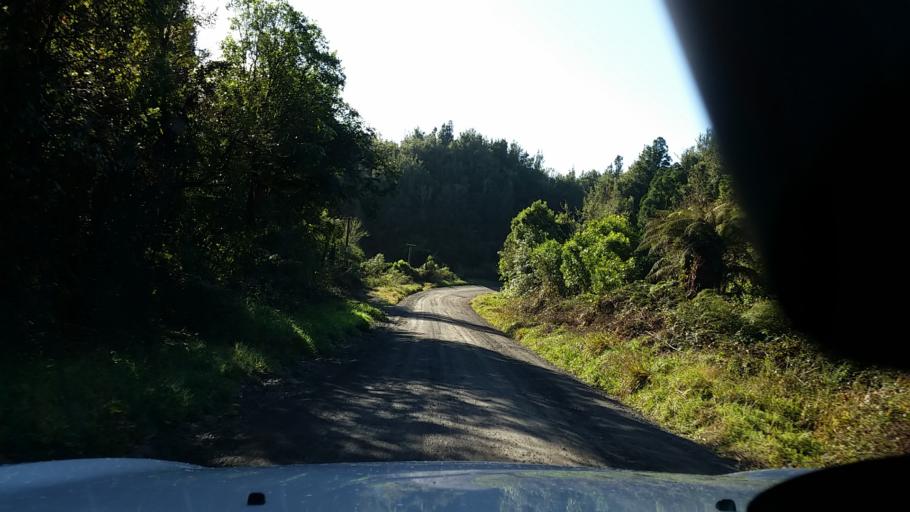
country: NZ
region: Bay of Plenty
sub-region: Kawerau District
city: Kawerau
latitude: -38.0179
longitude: 176.4821
